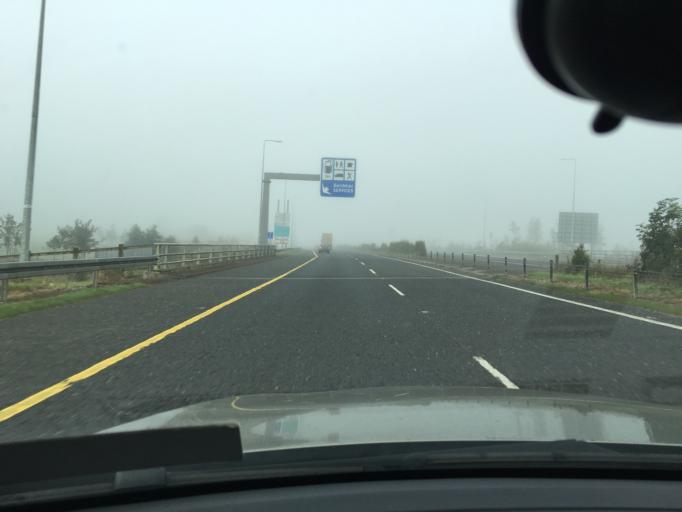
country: IE
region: Leinster
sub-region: An Mhi
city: Enfield
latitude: 53.4131
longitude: -6.8700
